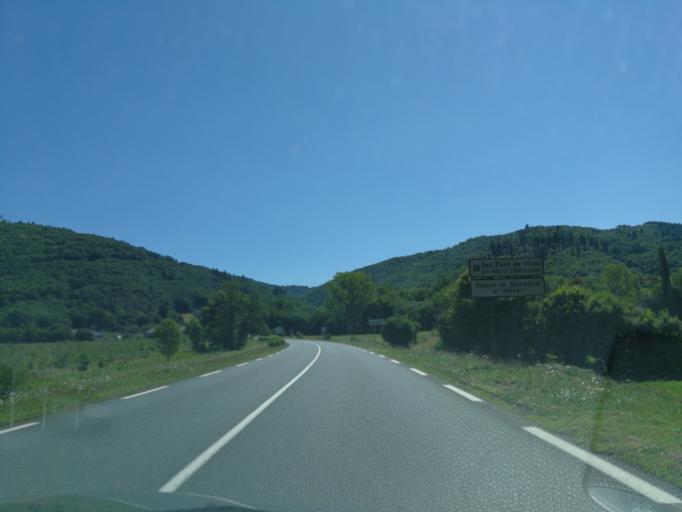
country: FR
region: Limousin
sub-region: Departement de la Correze
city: Argentat
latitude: 45.0856
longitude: 1.9387
